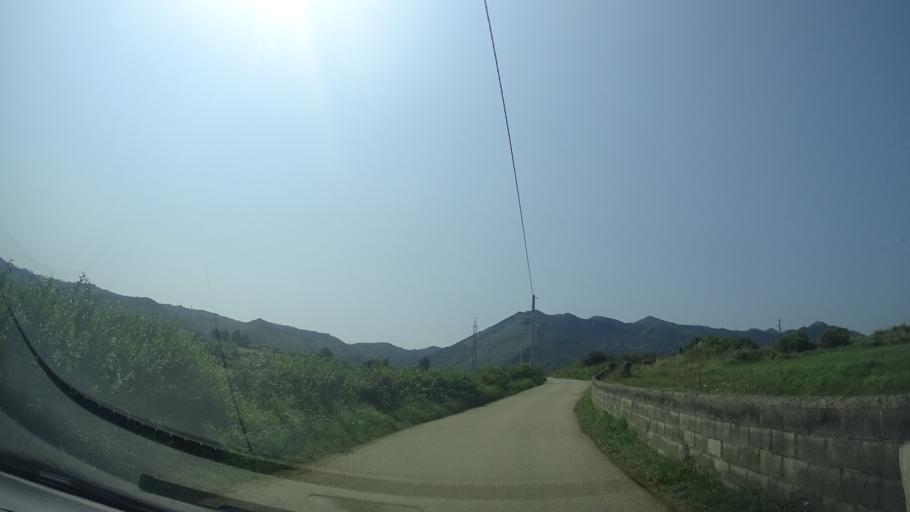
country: ES
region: Asturias
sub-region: Province of Asturias
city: Colunga
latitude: 43.4718
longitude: -5.2036
